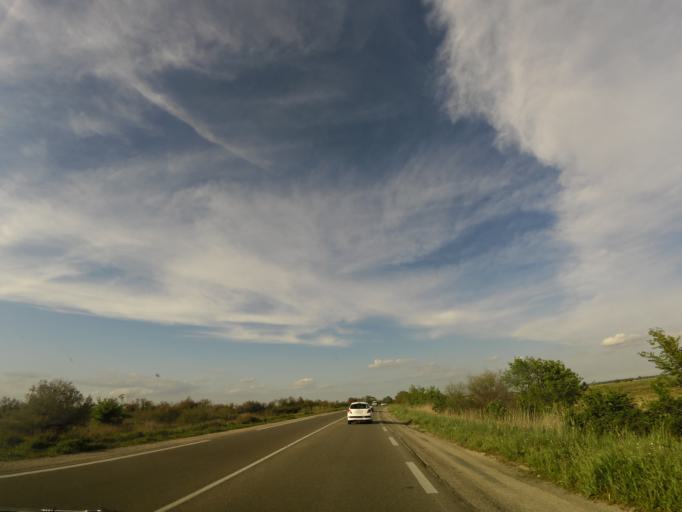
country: FR
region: Languedoc-Roussillon
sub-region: Departement de l'Herault
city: Saint-Just
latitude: 43.6158
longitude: 4.1130
